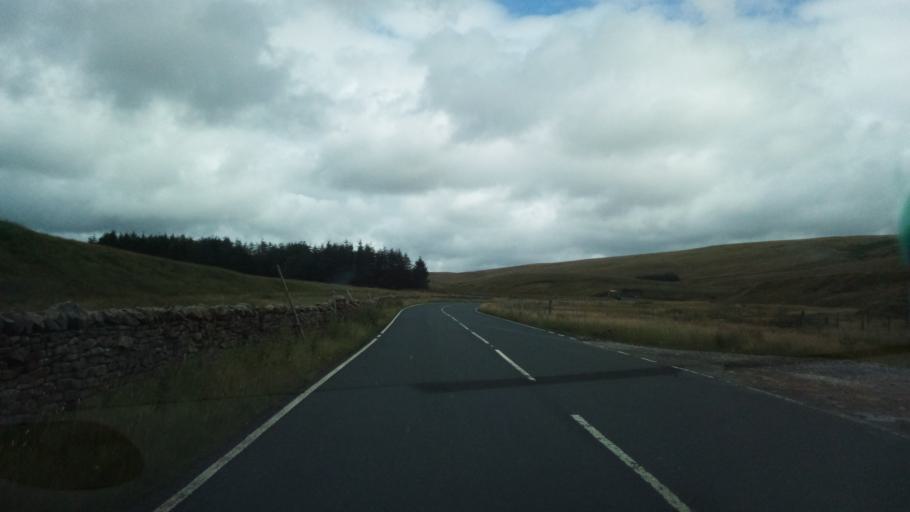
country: GB
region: England
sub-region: North Yorkshire
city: Ingleton
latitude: 54.2278
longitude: -2.3223
